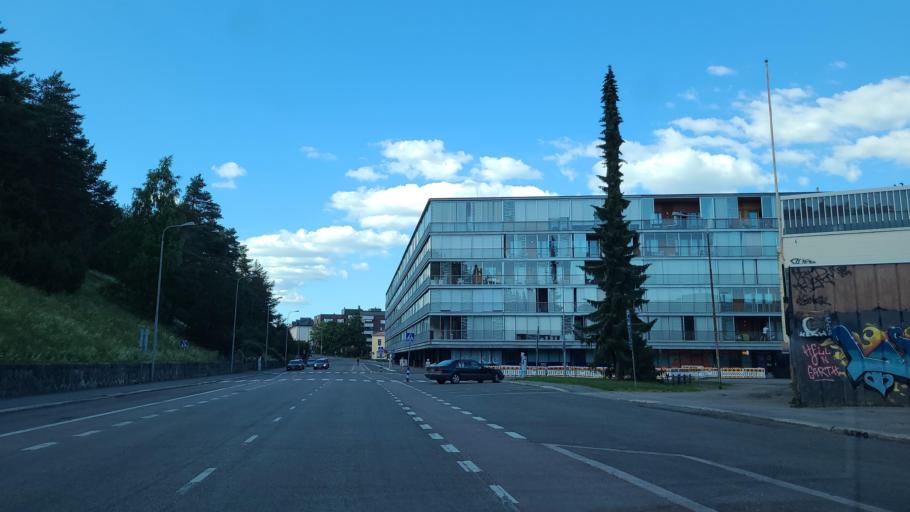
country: FI
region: Central Finland
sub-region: Jyvaeskylae
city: Jyvaeskylae
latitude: 62.2442
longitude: 25.7432
